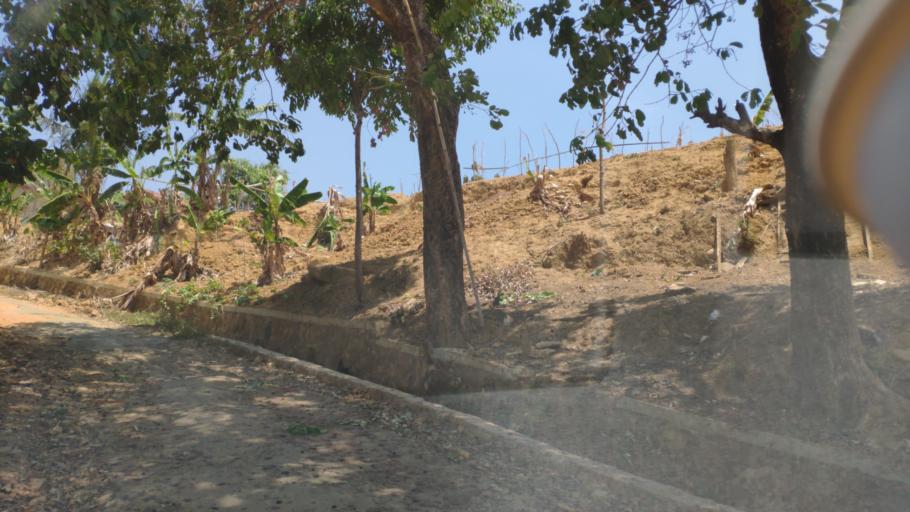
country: ID
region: Central Java
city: Guyangan
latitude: -6.9292
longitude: 111.1156
